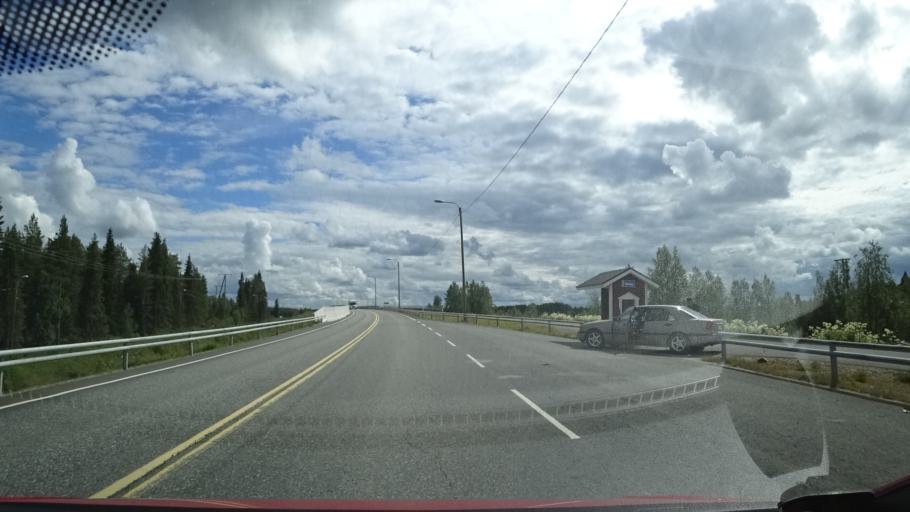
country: FI
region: Lapland
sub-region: Tunturi-Lappi
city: Kittilae
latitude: 67.4871
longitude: 24.9078
